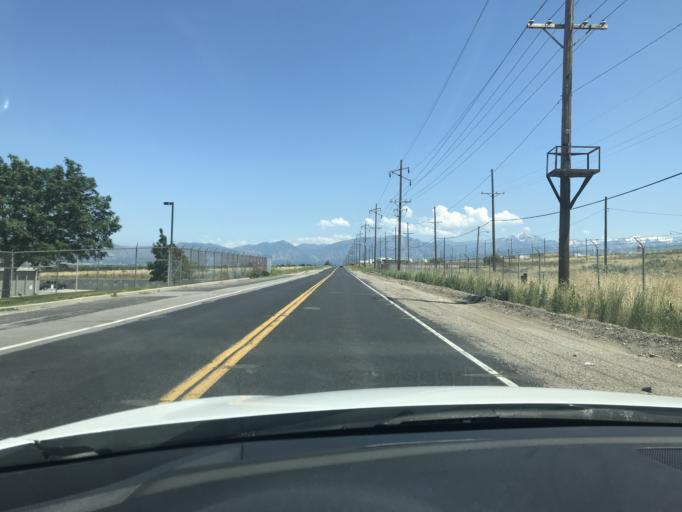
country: US
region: Utah
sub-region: Salt Lake County
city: Magna
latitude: 40.6820
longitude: -112.0768
